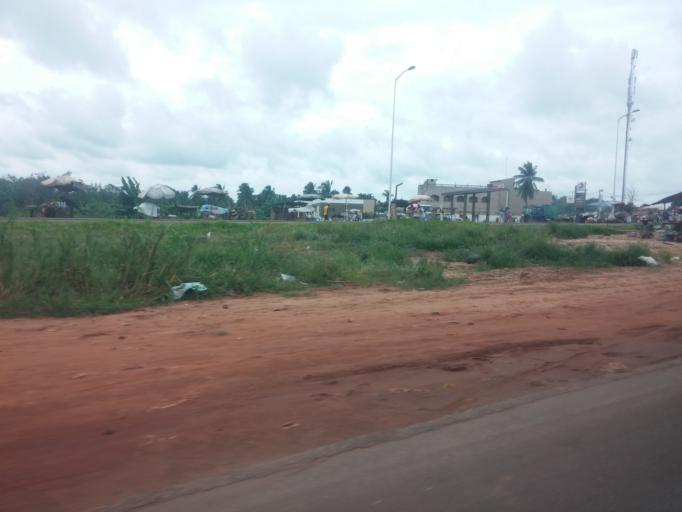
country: TG
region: Maritime
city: Tsevie
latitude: 6.3247
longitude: 1.2188
